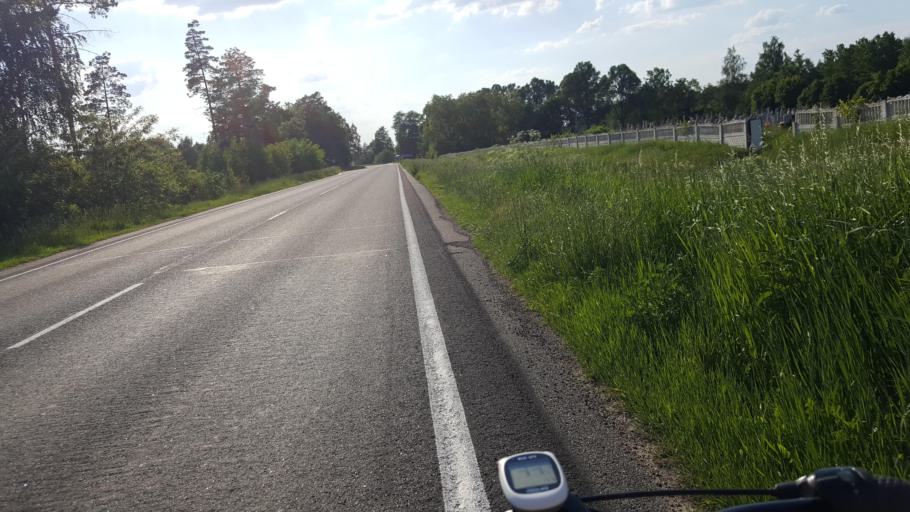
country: BY
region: Brest
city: Kamyanyets
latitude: 52.3997
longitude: 23.9033
